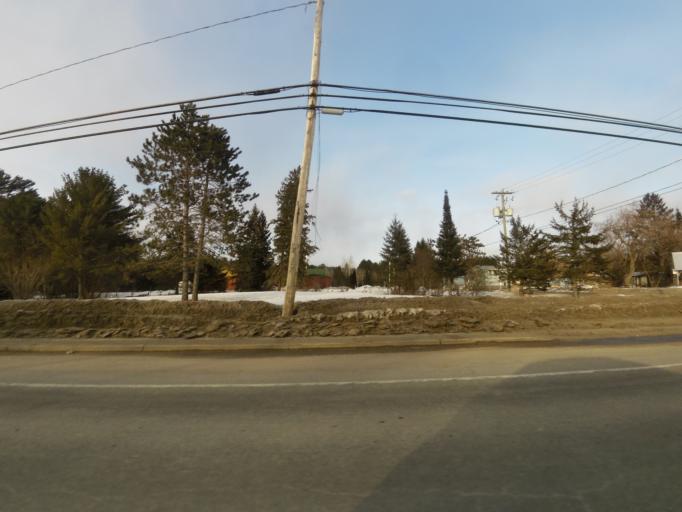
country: CA
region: Quebec
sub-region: Outaouais
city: Wakefield
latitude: 45.9487
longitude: -76.0160
